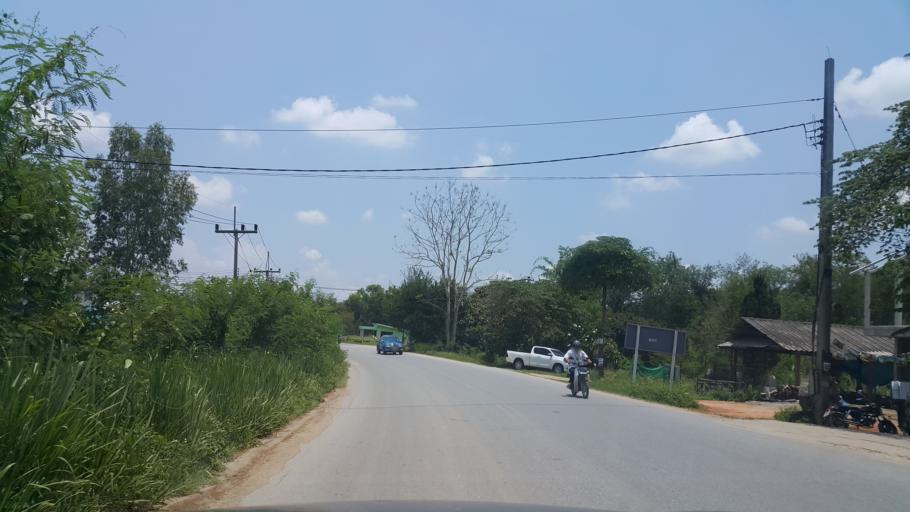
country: TH
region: Chiang Rai
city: Chiang Rai
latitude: 19.9348
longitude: 99.8121
